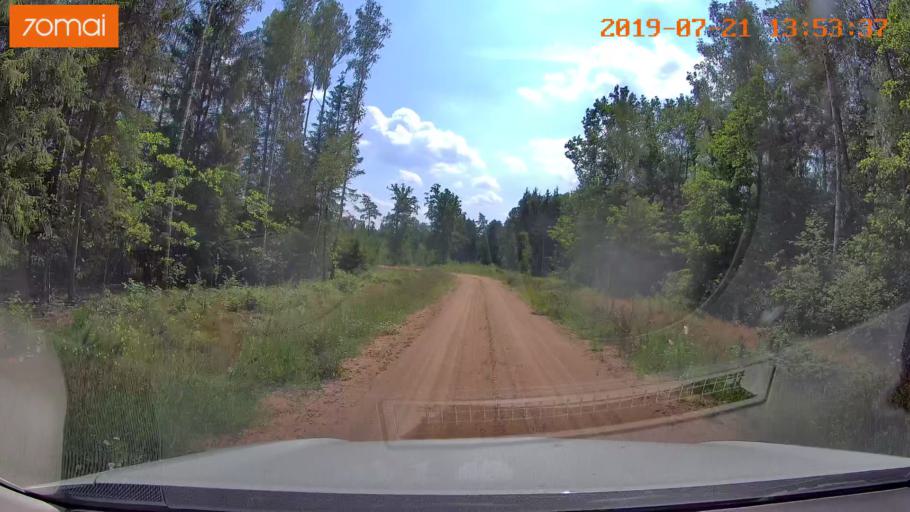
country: BY
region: Grodnenskaya
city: Lyubcha
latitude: 53.7779
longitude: 26.0646
